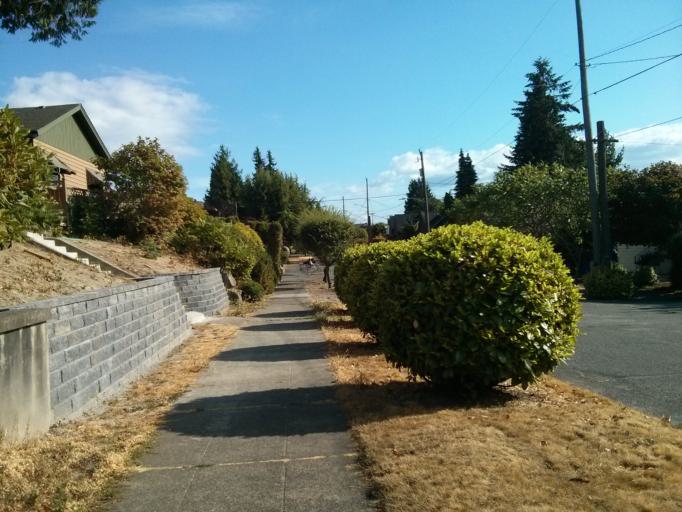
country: US
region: Washington
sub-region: King County
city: Seattle
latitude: 47.5836
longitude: -122.3918
